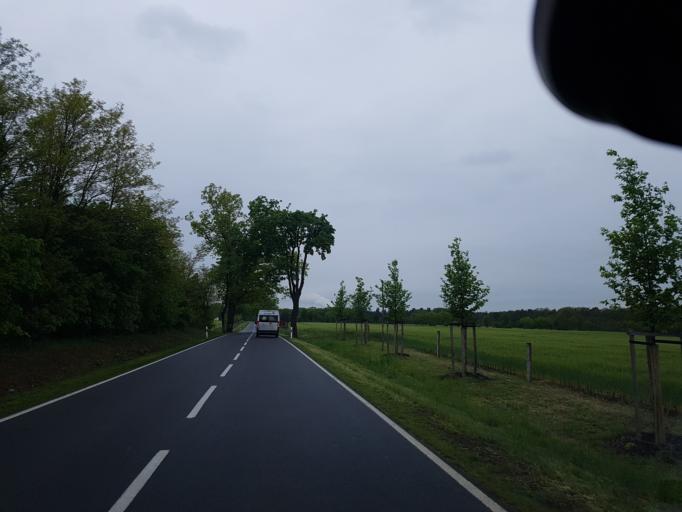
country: DE
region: Saxony
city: Gross Duben
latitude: 51.6181
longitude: 14.4913
